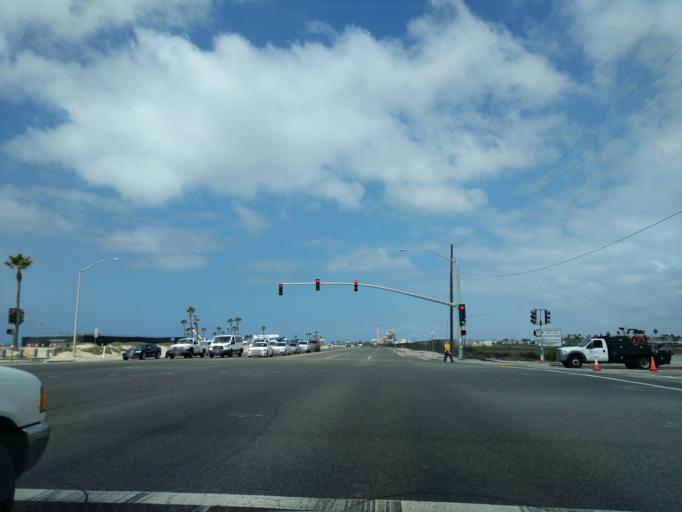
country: US
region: California
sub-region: Orange County
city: Newport Beach
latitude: 33.6352
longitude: -117.9639
